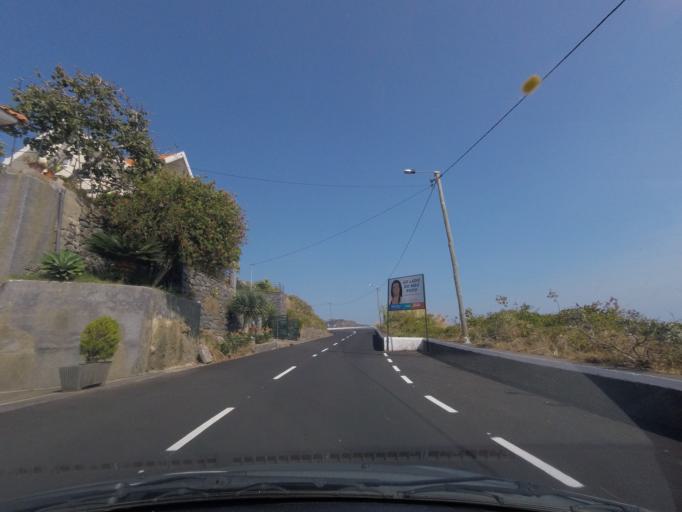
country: PT
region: Madeira
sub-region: Ribeira Brava
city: Campanario
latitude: 32.6662
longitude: -17.0499
